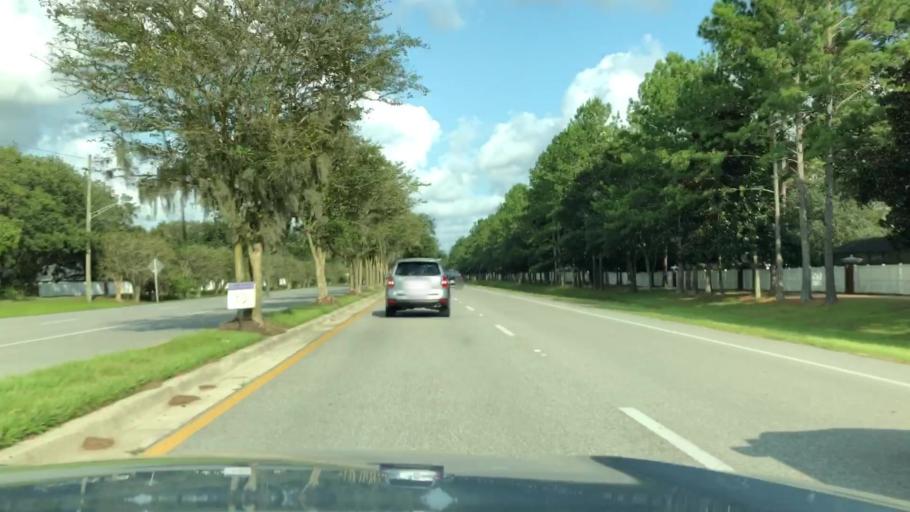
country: US
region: Florida
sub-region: Saint Johns County
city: Fruit Cove
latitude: 30.1197
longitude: -81.6166
